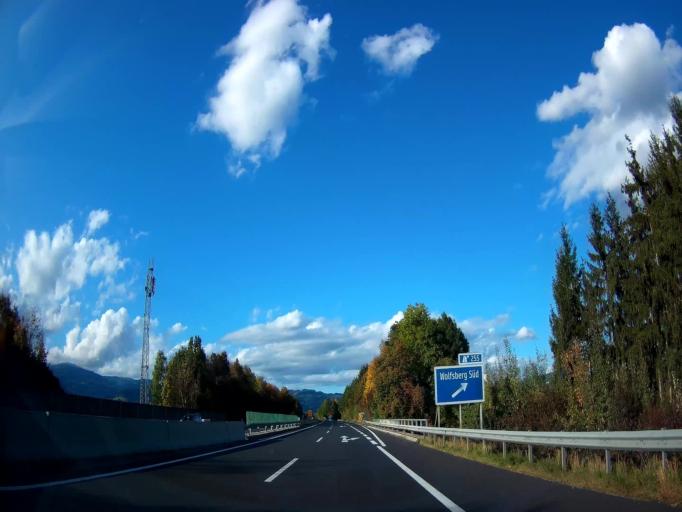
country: AT
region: Carinthia
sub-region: Politischer Bezirk Wolfsberg
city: Wolfsberg
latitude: 46.8182
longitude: 14.8224
